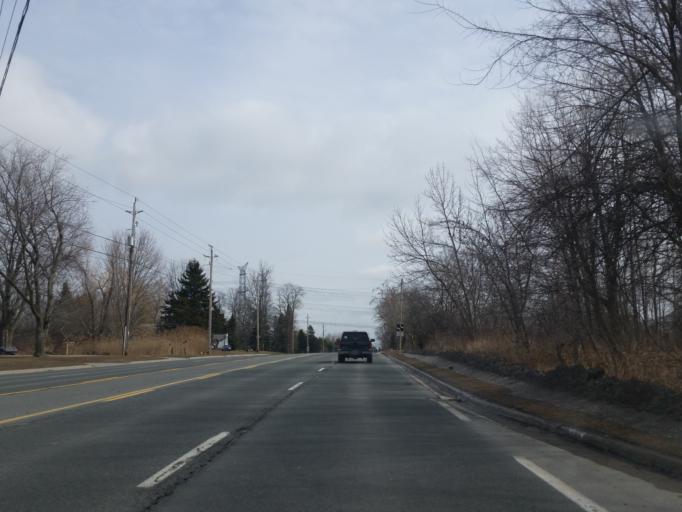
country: CA
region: Ontario
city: Oshawa
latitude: 43.9138
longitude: -78.7458
